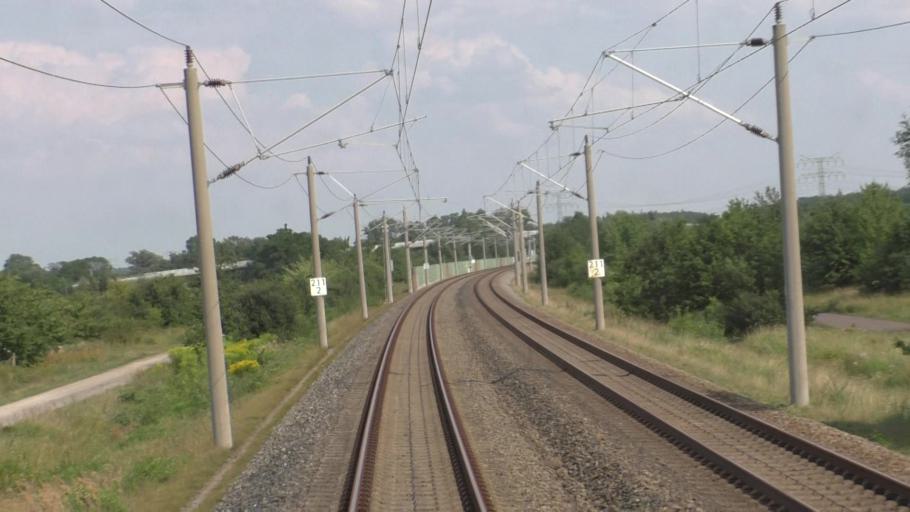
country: DE
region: Saxony-Anhalt
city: Uenglingen
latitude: 52.5818
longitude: 11.7748
